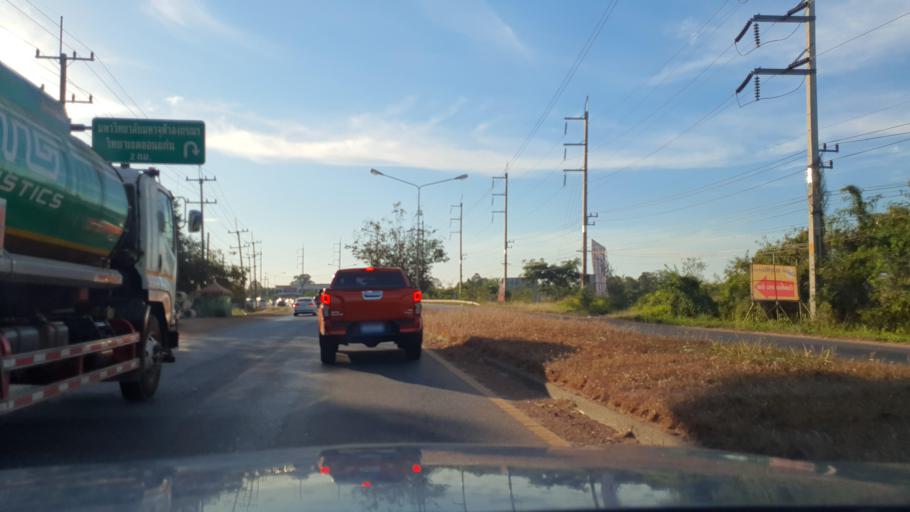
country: TH
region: Khon Kaen
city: Khon Kaen
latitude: 16.4466
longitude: 102.9506
